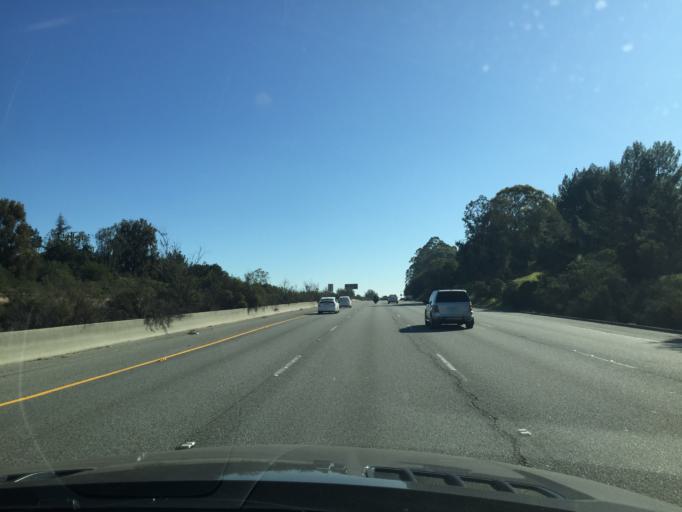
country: US
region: California
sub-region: Santa Clara County
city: Loyola
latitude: 37.3398
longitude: -122.0881
